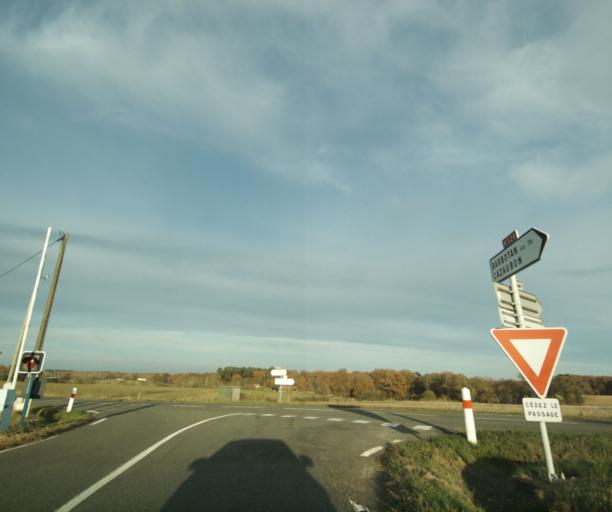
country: FR
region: Aquitaine
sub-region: Departement des Landes
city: Gabarret
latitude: 43.9693
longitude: 0.0056
